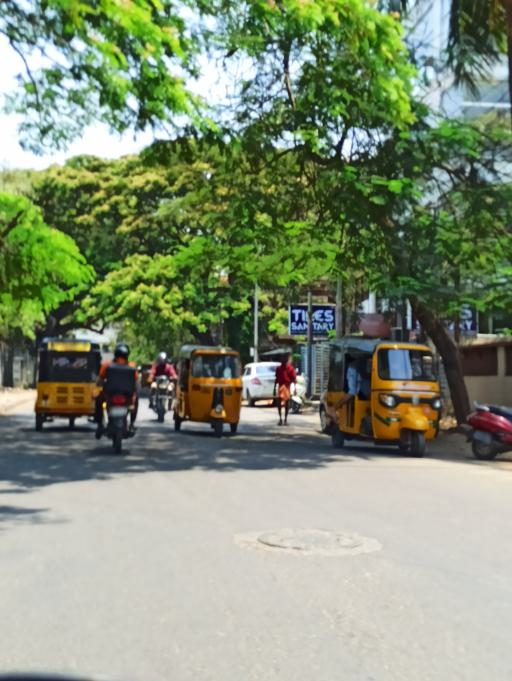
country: IN
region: Tamil Nadu
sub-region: Chennai
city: Chetput
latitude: 13.0717
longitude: 80.2320
